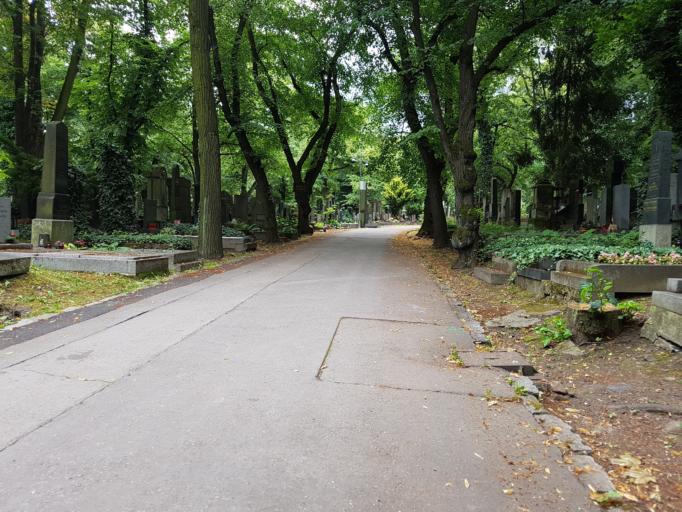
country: CZ
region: Praha
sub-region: Praha 8
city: Karlin
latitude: 50.0800
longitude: 14.4709
